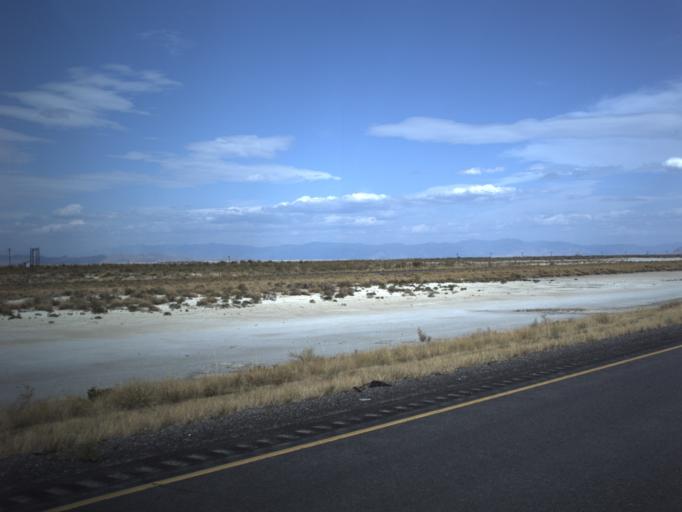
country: US
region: Utah
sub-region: Tooele County
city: Grantsville
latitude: 40.7047
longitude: -112.5124
